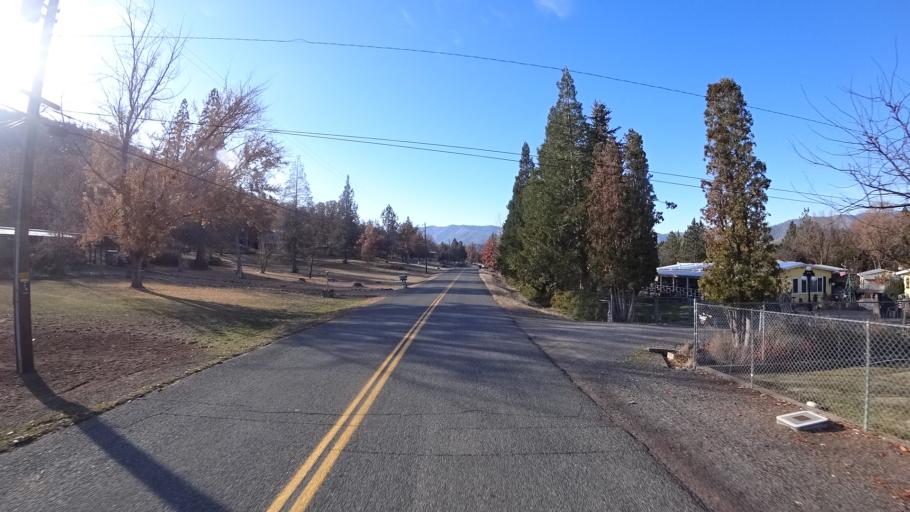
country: US
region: California
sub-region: Siskiyou County
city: Yreka
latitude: 41.6989
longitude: -122.6326
